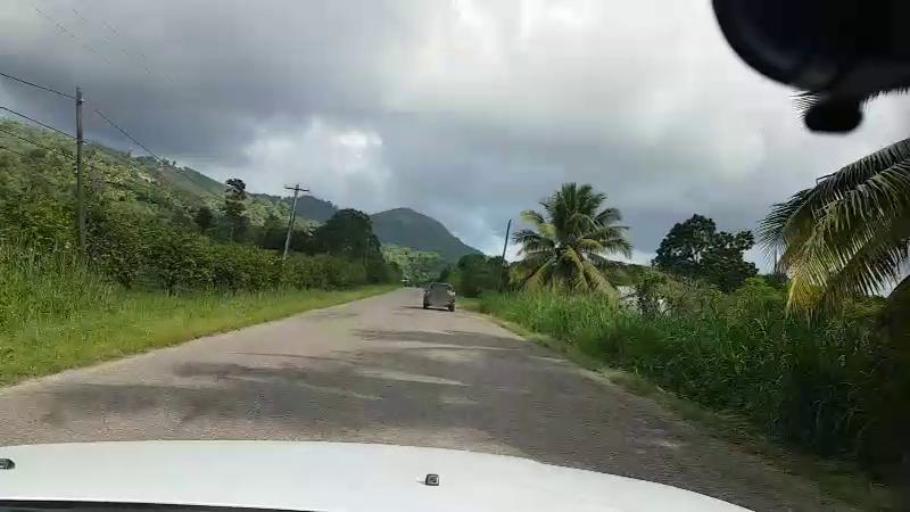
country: BZ
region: Stann Creek
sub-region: Dangriga
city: Dangriga
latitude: 16.9977
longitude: -88.4138
